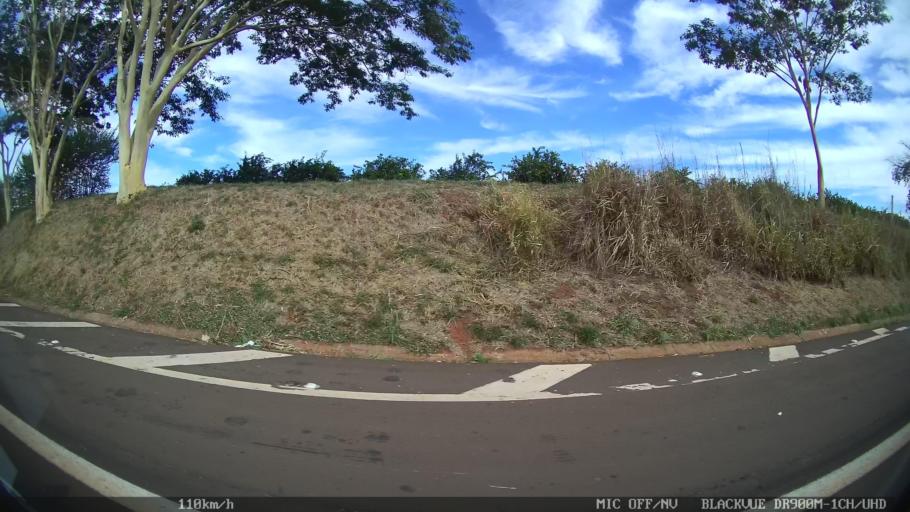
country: BR
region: Sao Paulo
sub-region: Taquaritinga
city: Taquaritinga
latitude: -21.4561
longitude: -48.6271
